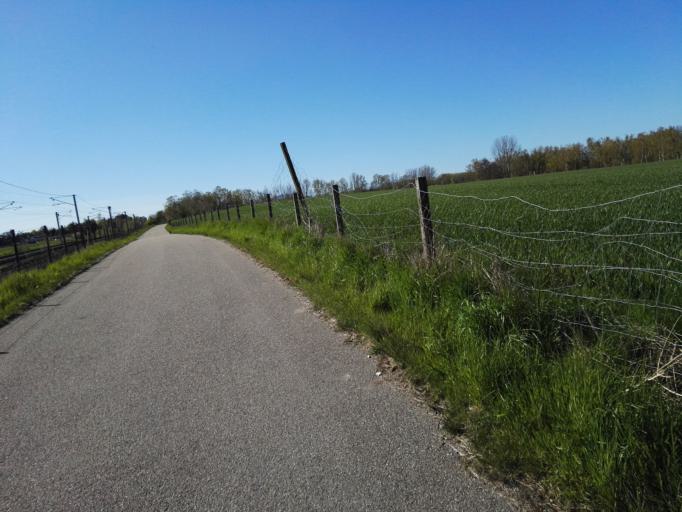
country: DK
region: Capital Region
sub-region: Egedal Kommune
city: Stenlose
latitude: 55.7555
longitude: 12.2075
